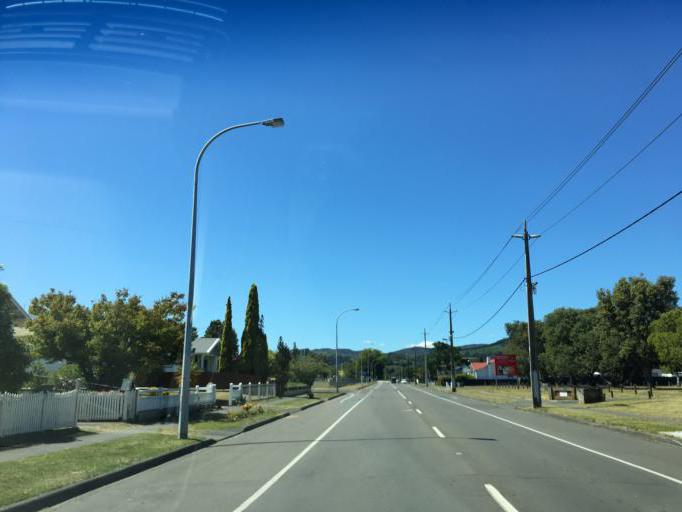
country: NZ
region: Gisborne
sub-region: Gisborne District
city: Gisborne
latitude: -38.6593
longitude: 178.0083
